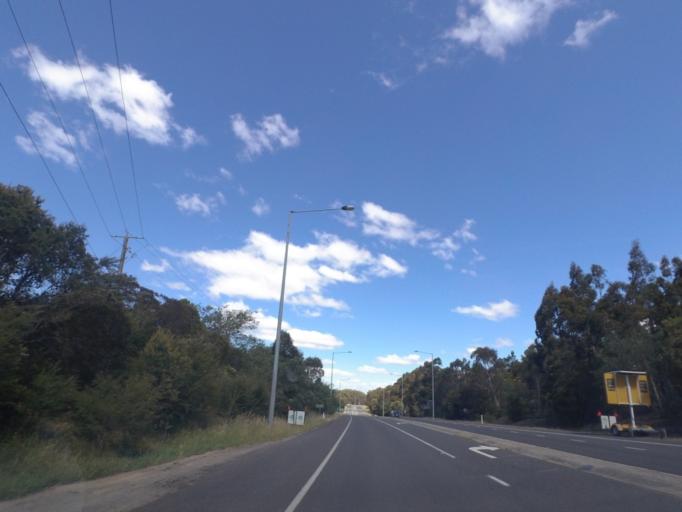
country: AU
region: Victoria
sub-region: Hume
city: Sunbury
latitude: -37.4159
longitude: 144.5470
